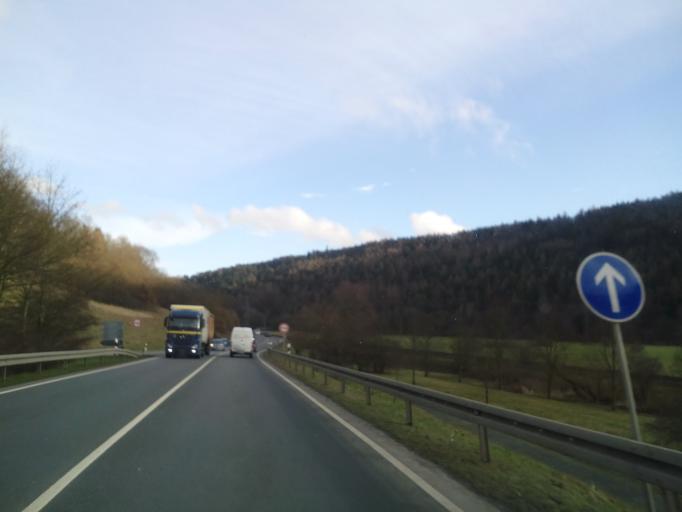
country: DE
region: Bavaria
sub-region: Upper Franconia
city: Kulmbach
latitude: 50.1121
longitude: 11.4858
